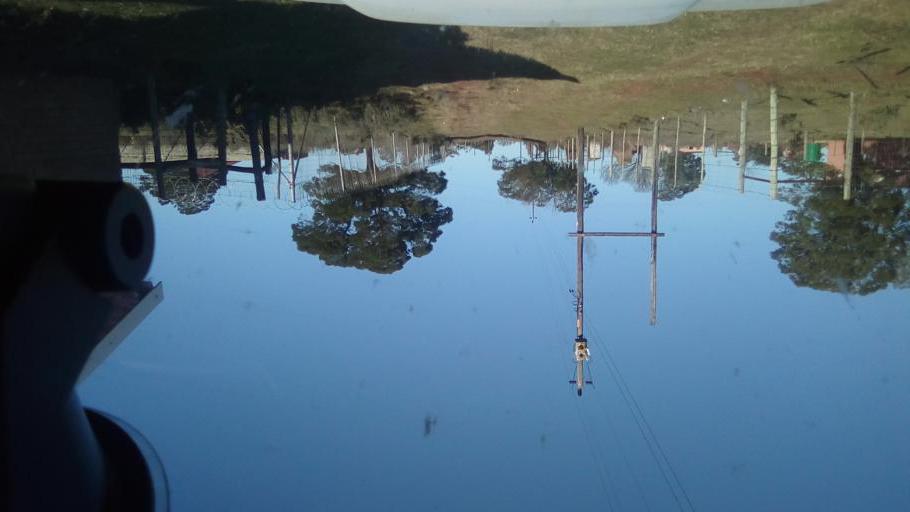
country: ZA
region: Eastern Cape
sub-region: Buffalo City Metropolitan Municipality
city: Bhisho
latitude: -32.9468
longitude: 27.2936
